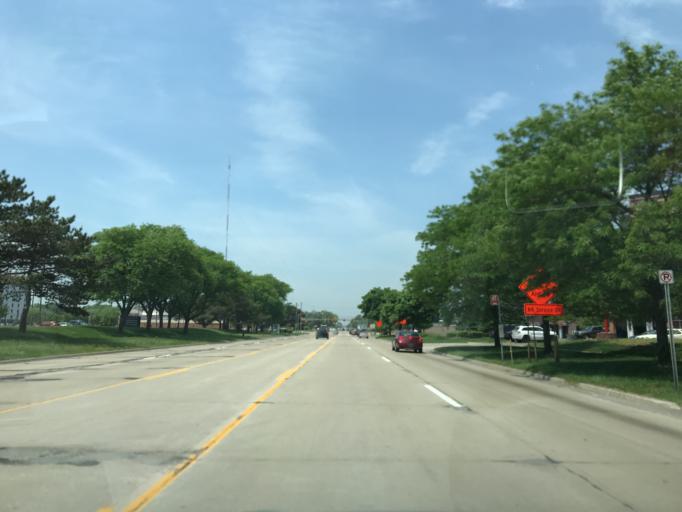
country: US
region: Michigan
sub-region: Oakland County
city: Southfield
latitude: 42.4730
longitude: -83.2373
